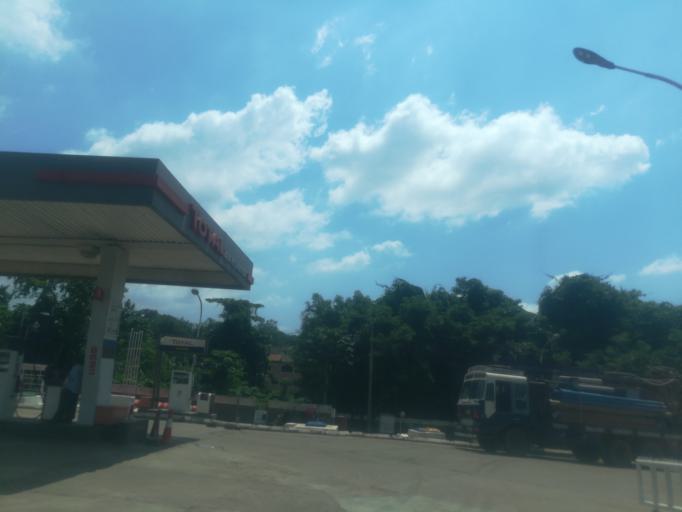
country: NG
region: Oyo
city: Ibadan
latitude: 7.3827
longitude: 3.8711
